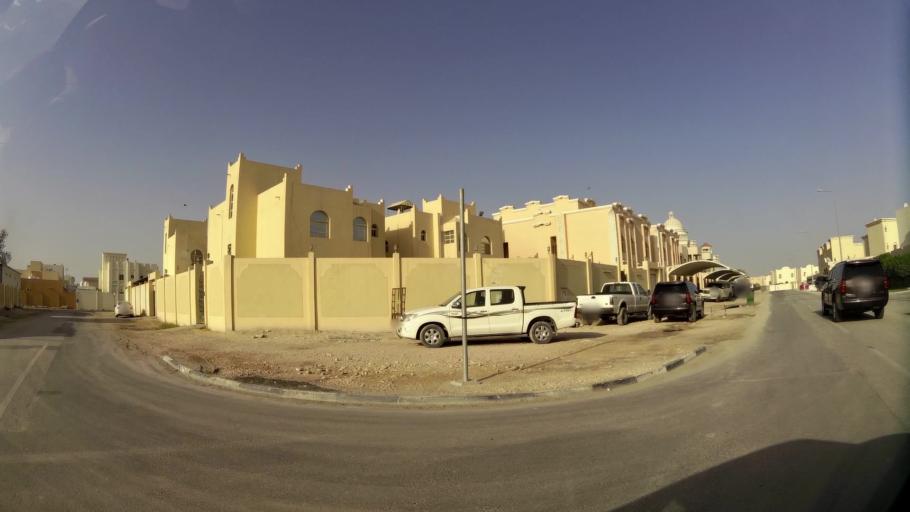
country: QA
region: Baladiyat ar Rayyan
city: Ar Rayyan
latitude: 25.3386
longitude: 51.4366
